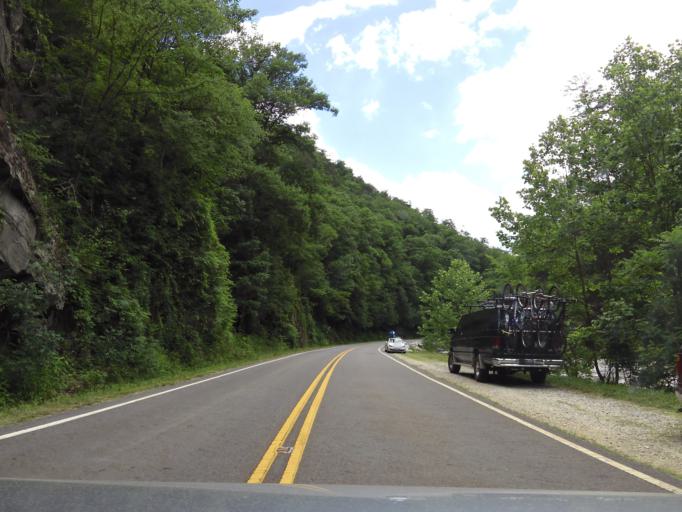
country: US
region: North Carolina
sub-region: Graham County
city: Robbinsville
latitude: 35.4405
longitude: -83.9288
